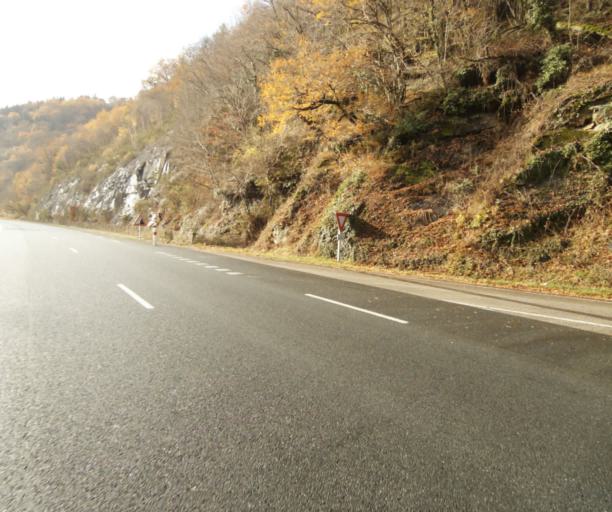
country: FR
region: Limousin
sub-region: Departement de la Correze
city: Cornil
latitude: 45.2123
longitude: 1.6863
